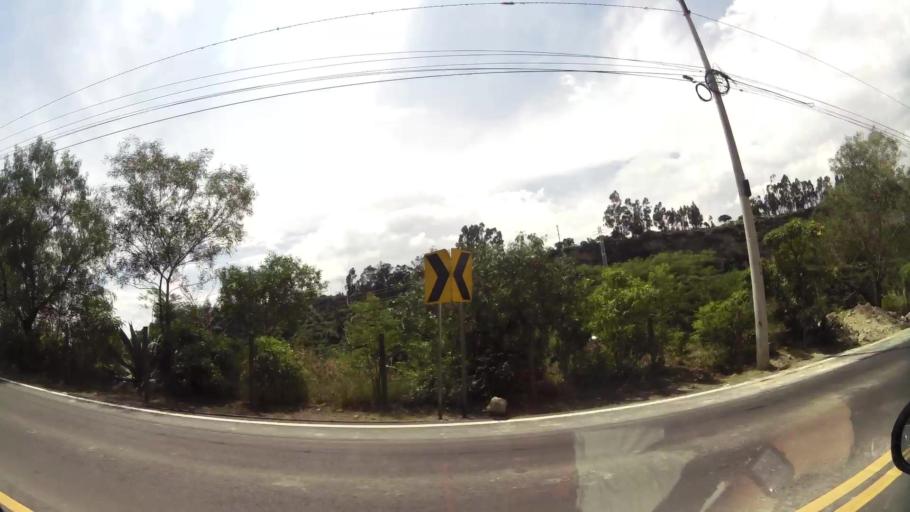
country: EC
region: Pichincha
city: Sangolqui
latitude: -0.2043
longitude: -78.3722
